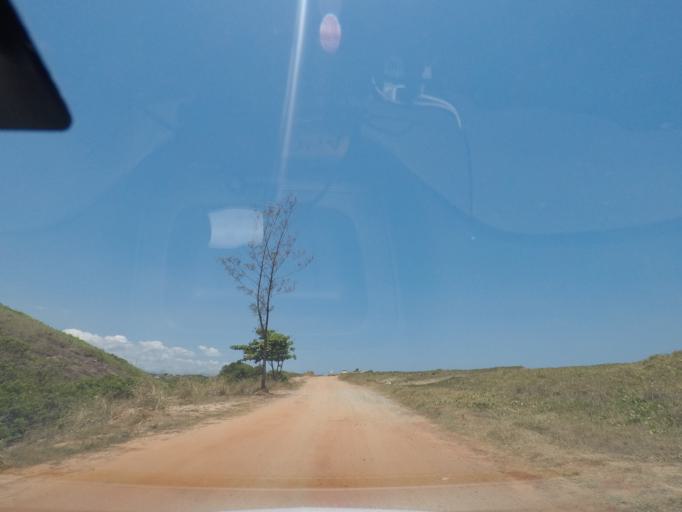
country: BR
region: Rio de Janeiro
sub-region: Niteroi
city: Niteroi
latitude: -22.9689
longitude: -43.0017
